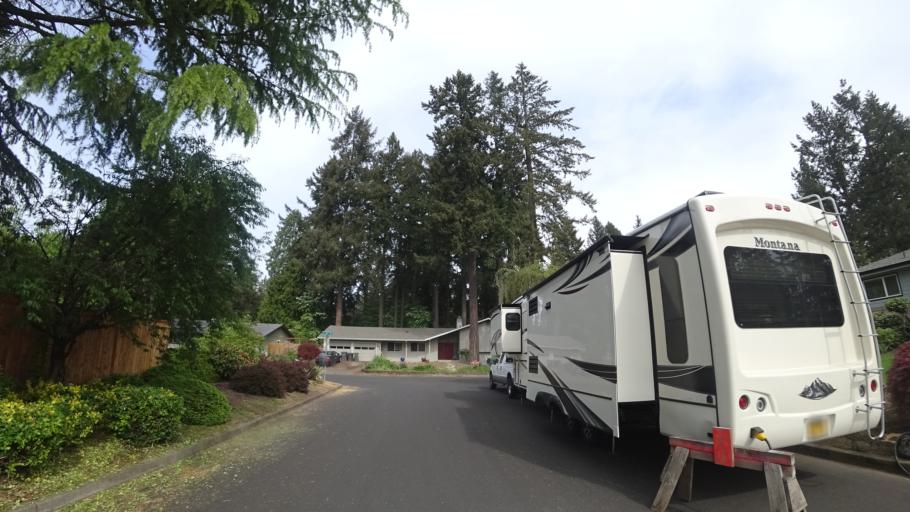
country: US
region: Oregon
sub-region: Washington County
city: Hillsboro
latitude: 45.5085
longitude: -122.9451
